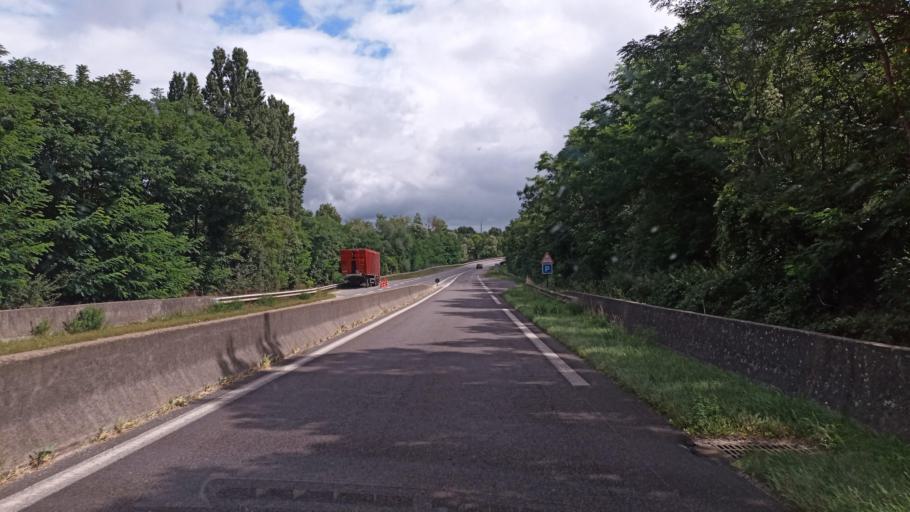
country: FR
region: Ile-de-France
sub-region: Departement de Seine-et-Marne
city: Moret-sur-Loing
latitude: 48.3659
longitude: 2.8201
